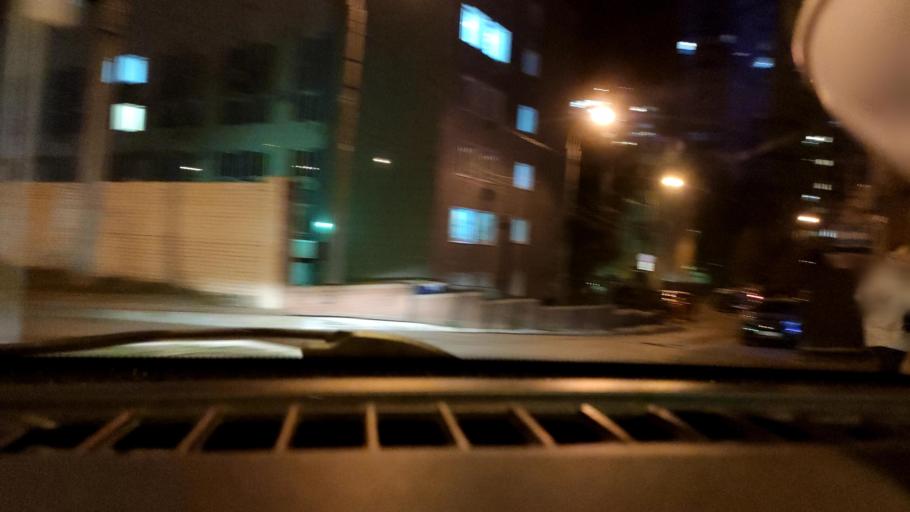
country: RU
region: Samara
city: Samara
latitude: 53.2197
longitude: 50.1554
